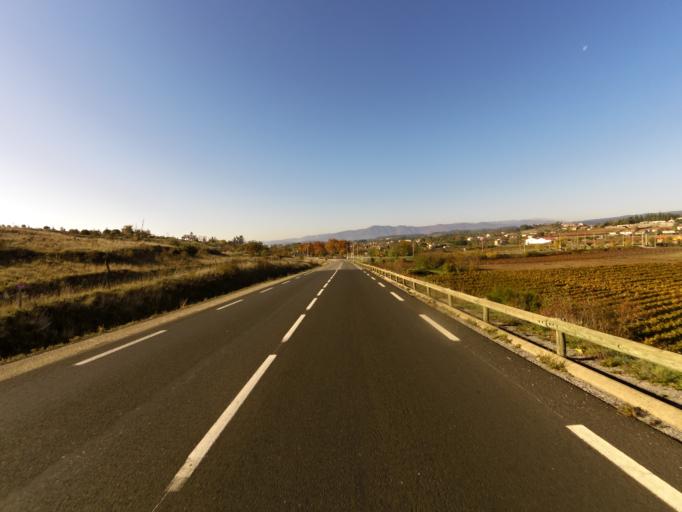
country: FR
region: Rhone-Alpes
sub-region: Departement de l'Ardeche
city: Lablachere
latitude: 44.4599
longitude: 4.2227
